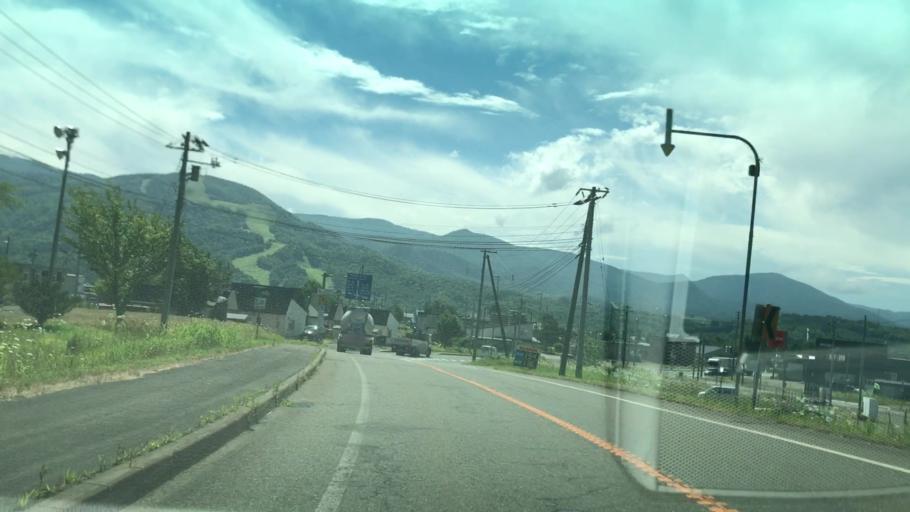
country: JP
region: Hokkaido
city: Shimo-furano
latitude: 42.8832
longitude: 142.4345
